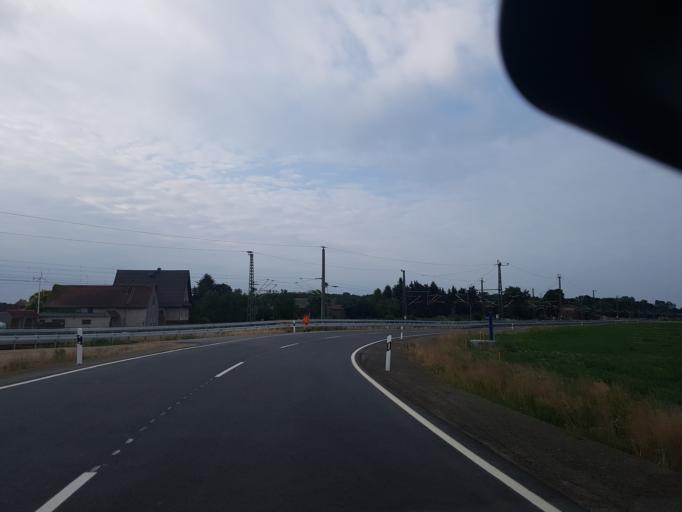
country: DE
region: Brandenburg
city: Schonewalde
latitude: 51.7041
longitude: 13.5962
